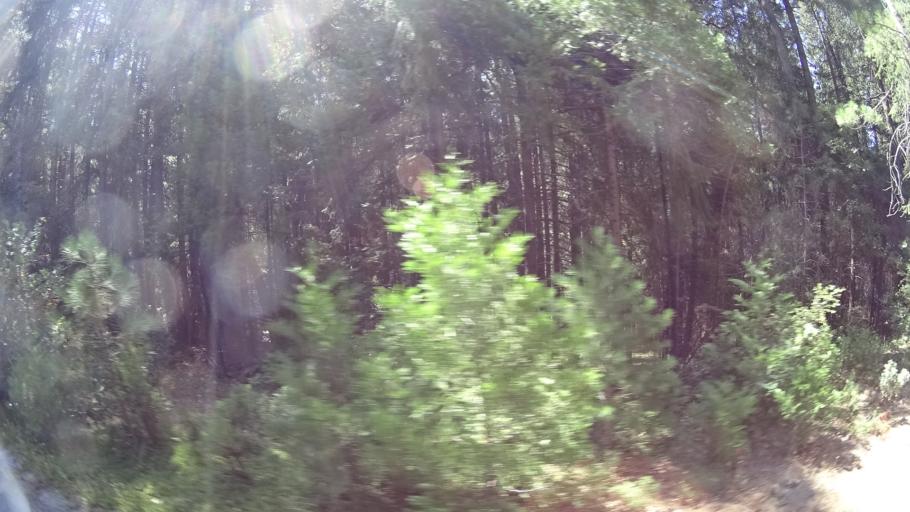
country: US
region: California
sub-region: Amador County
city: Pioneer
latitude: 38.4246
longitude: -120.4895
